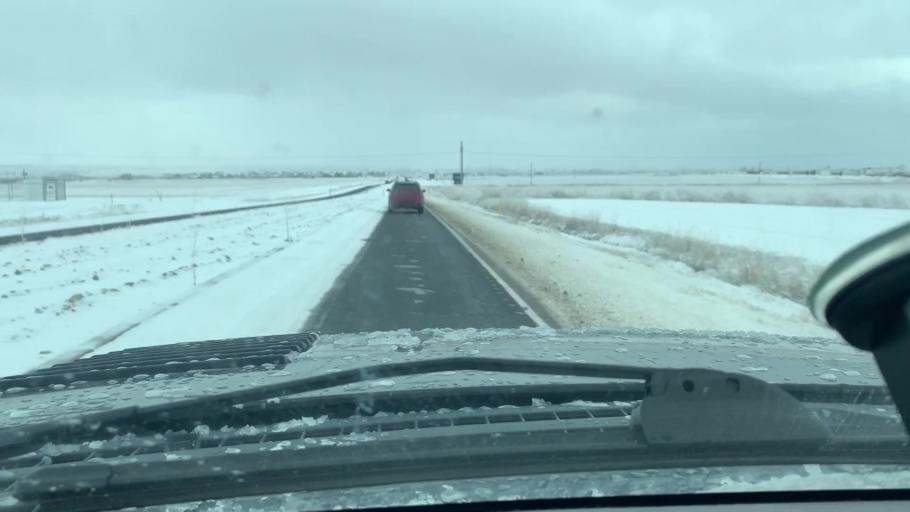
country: US
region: Colorado
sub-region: Weld County
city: Mead
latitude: 40.1996
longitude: -104.9702
